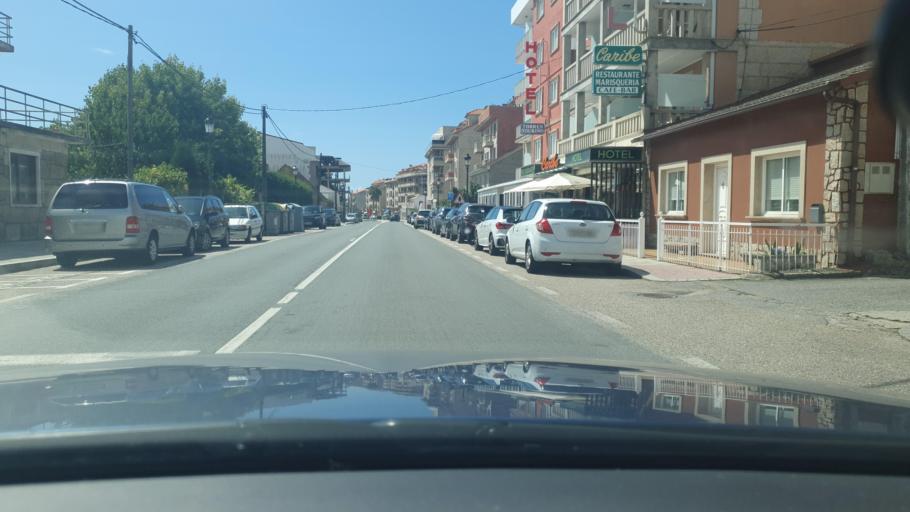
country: ES
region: Galicia
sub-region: Provincia de Pontevedra
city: O Grove
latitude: 42.4459
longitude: -8.8609
